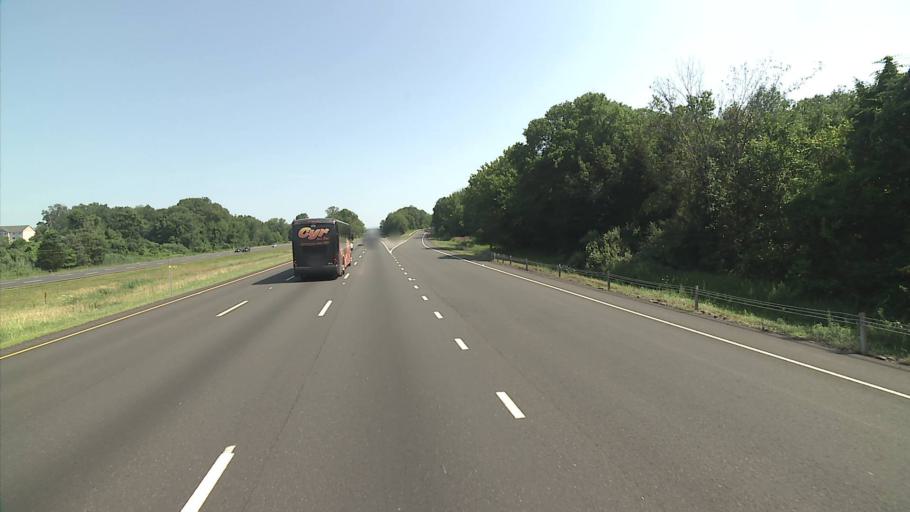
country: US
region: Connecticut
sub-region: New Haven County
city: Wallingford Center
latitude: 41.4758
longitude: -72.7713
